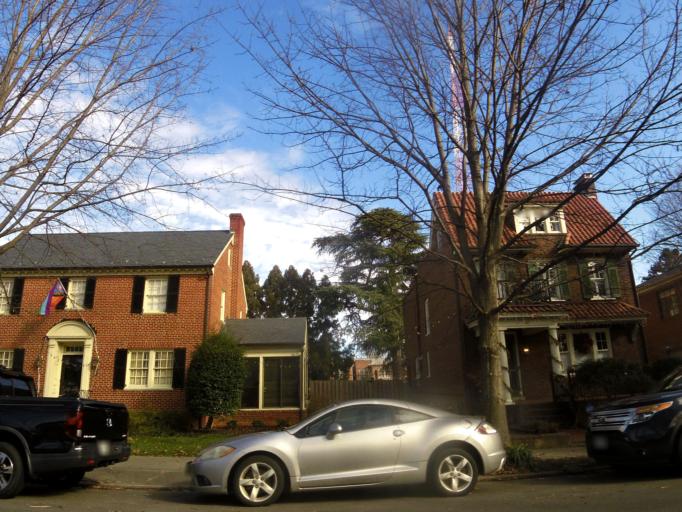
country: US
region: Virginia
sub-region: City of Richmond
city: Richmond
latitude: 37.5651
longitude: -77.4787
